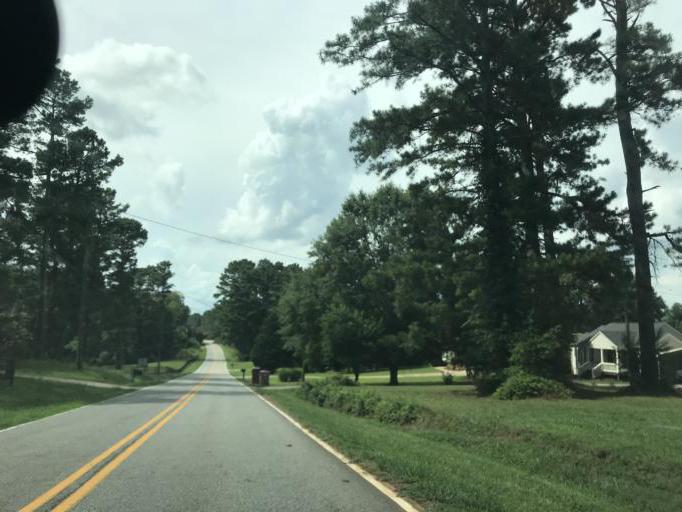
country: US
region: Georgia
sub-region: Forsyth County
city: Cumming
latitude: 34.2190
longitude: -84.2389
